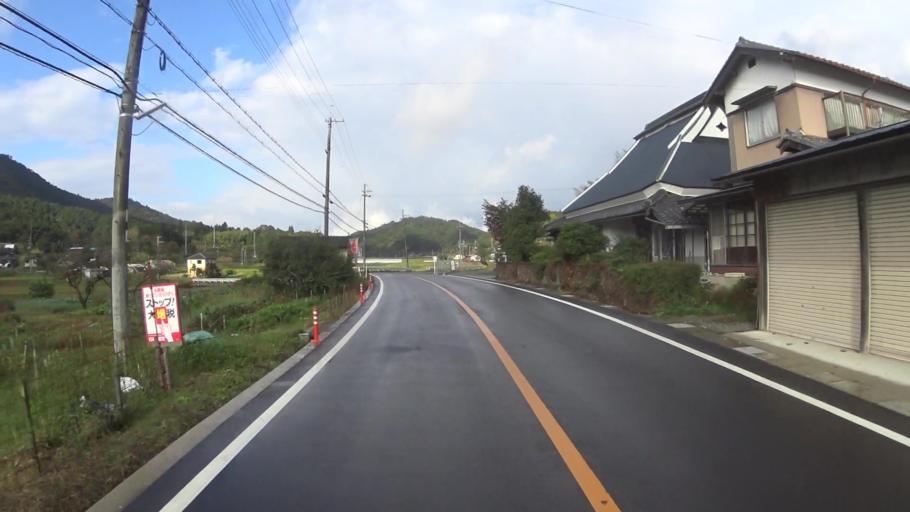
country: JP
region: Kyoto
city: Ayabe
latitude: 35.3647
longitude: 135.2015
